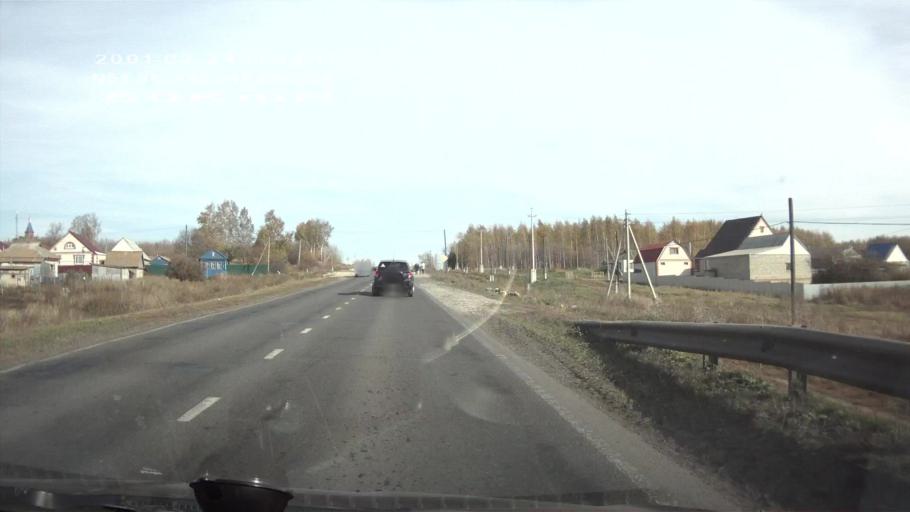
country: RU
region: Mordoviya
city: Atyashevo
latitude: 54.5624
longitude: 45.9806
